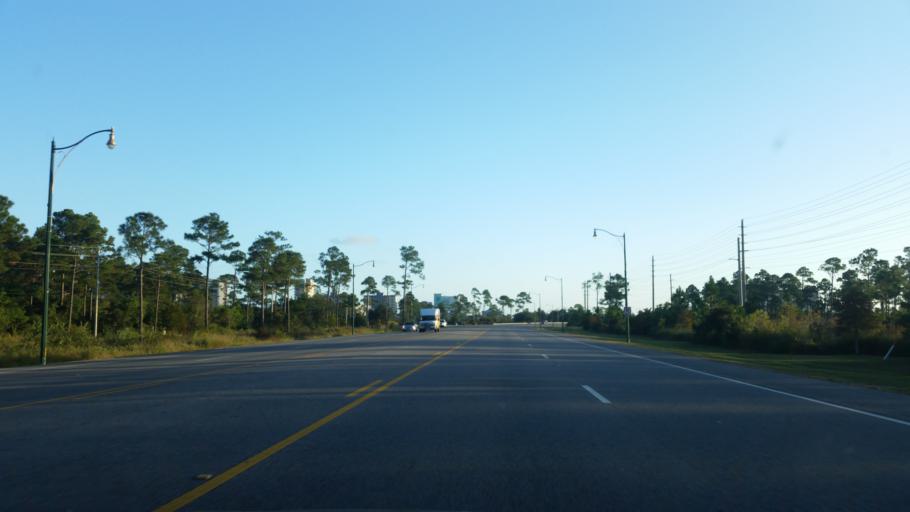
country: US
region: Alabama
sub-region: Baldwin County
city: Orange Beach
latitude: 30.2779
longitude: -87.5809
